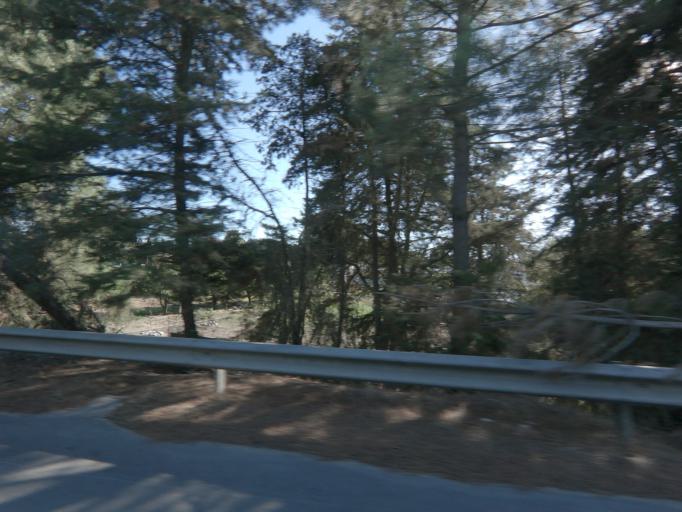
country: PT
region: Setubal
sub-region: Palmela
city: Pinhal Novo
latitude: 38.6155
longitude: -8.9523
